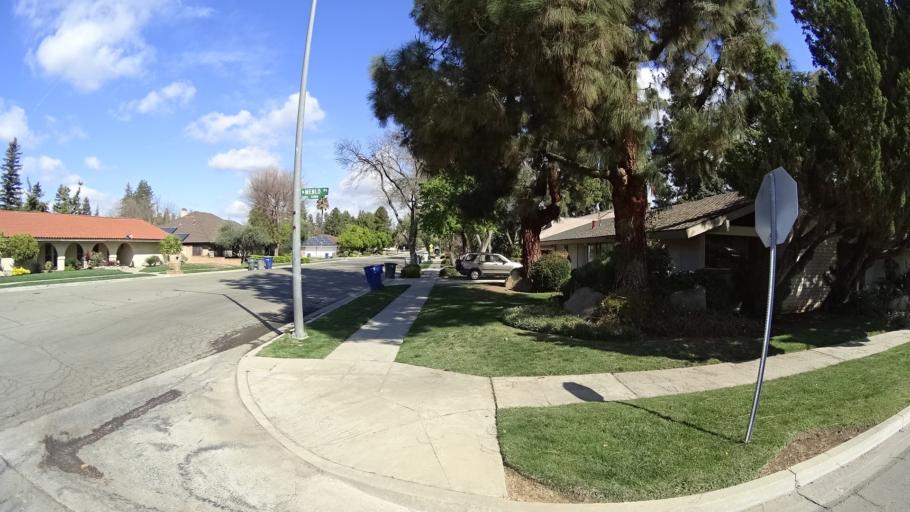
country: US
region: California
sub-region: Fresno County
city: Fresno
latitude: 36.8308
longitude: -119.8533
